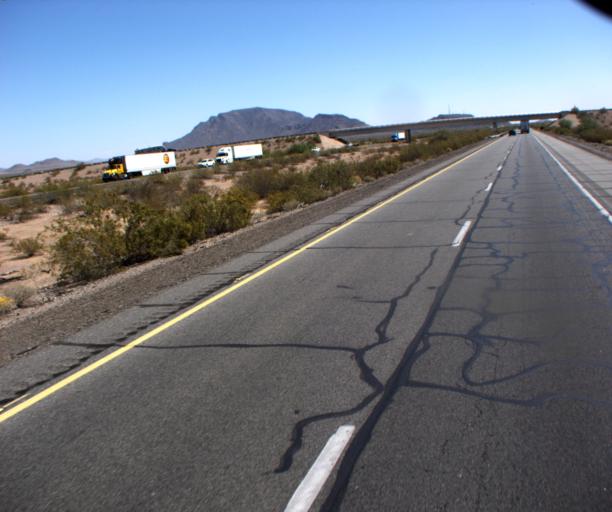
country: US
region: Arizona
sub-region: La Paz County
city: Salome
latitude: 33.5382
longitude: -113.1589
